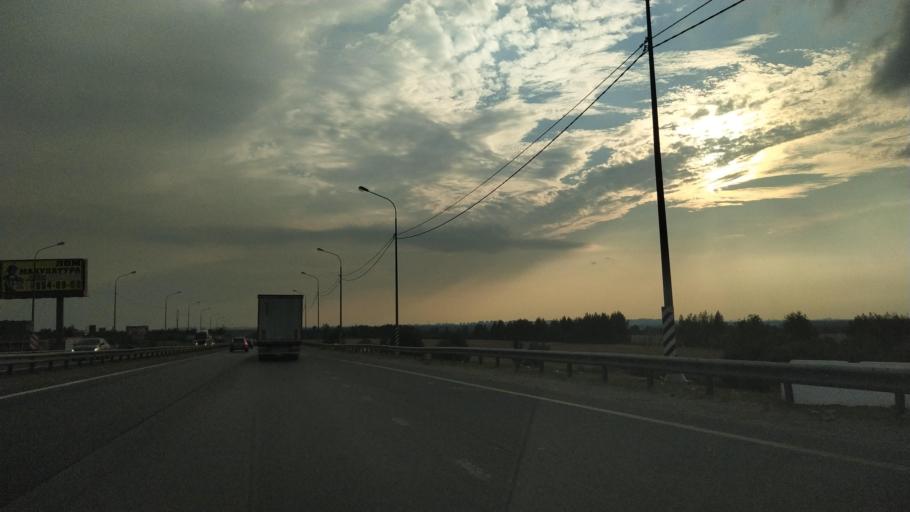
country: RU
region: Leningrad
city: Koltushi
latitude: 59.8961
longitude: 30.6711
